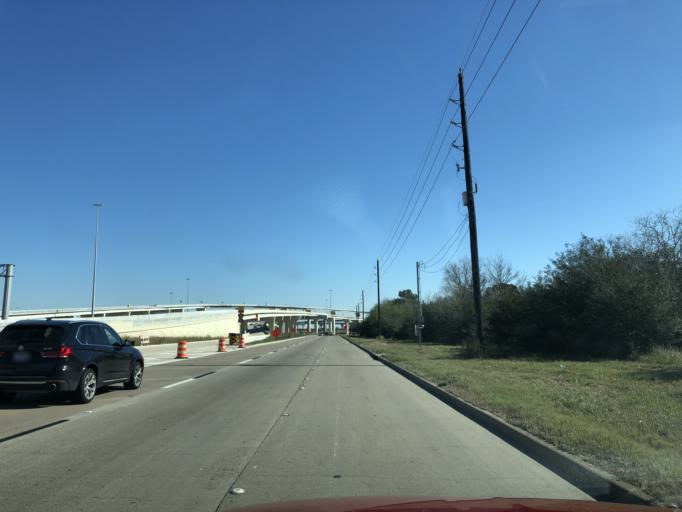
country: US
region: Texas
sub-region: Brazoria County
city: Brookside Village
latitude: 29.5965
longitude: -95.3949
